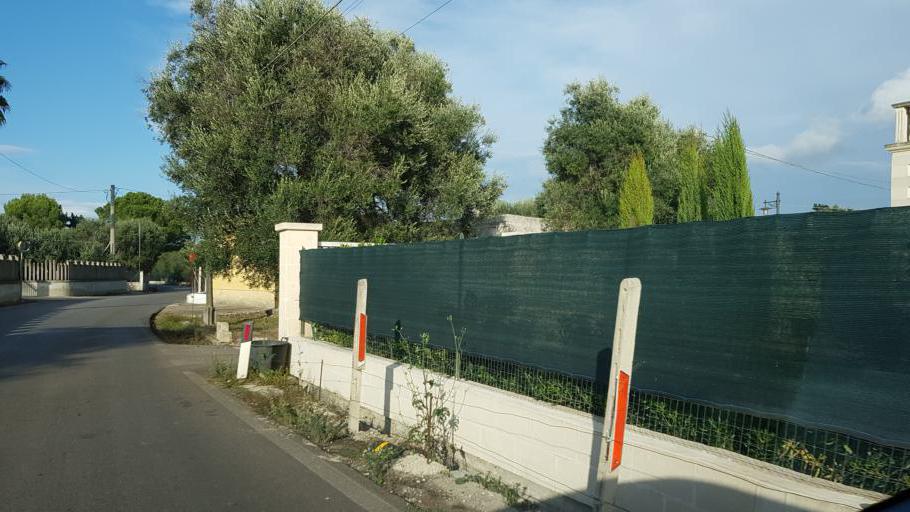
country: IT
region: Apulia
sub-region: Provincia di Brindisi
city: Oria
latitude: 40.5153
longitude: 17.6506
